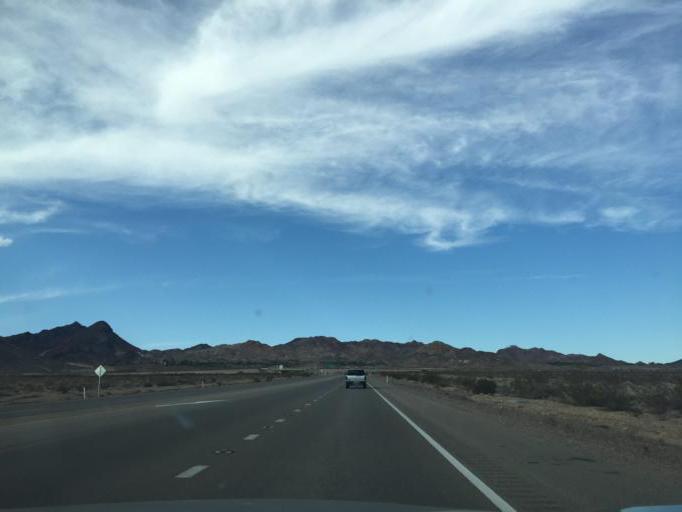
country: US
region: Nevada
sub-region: Clark County
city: Boulder City
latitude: 35.9605
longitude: -114.8971
